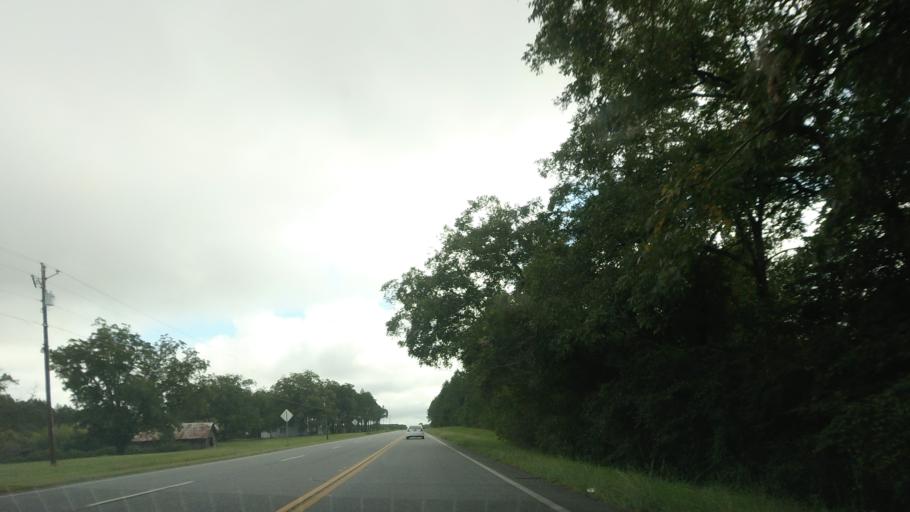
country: US
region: Georgia
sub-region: Laurens County
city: Dublin
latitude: 32.5504
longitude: -83.0071
